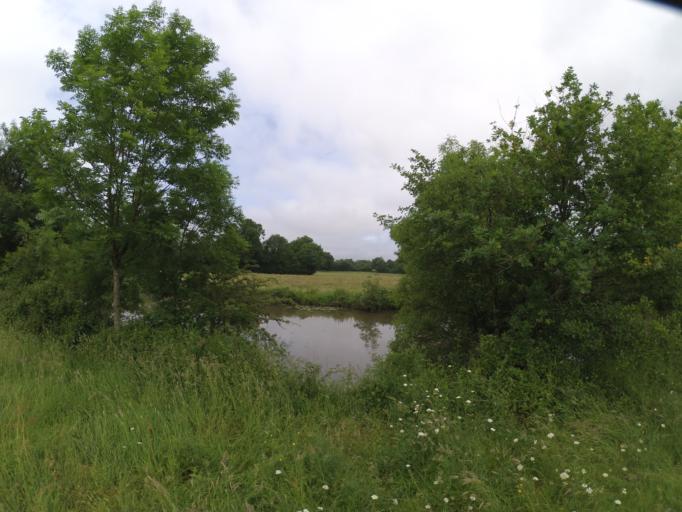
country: FR
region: Pays de la Loire
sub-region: Departement de la Vendee
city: Nesmy
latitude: 46.6208
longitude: -1.4148
